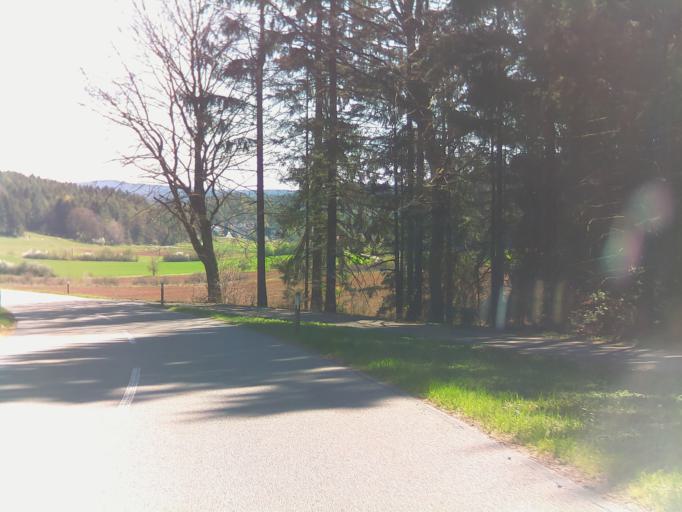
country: DE
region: Bavaria
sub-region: Upper Palatinate
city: Lauterhofen
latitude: 49.4096
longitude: 11.6074
